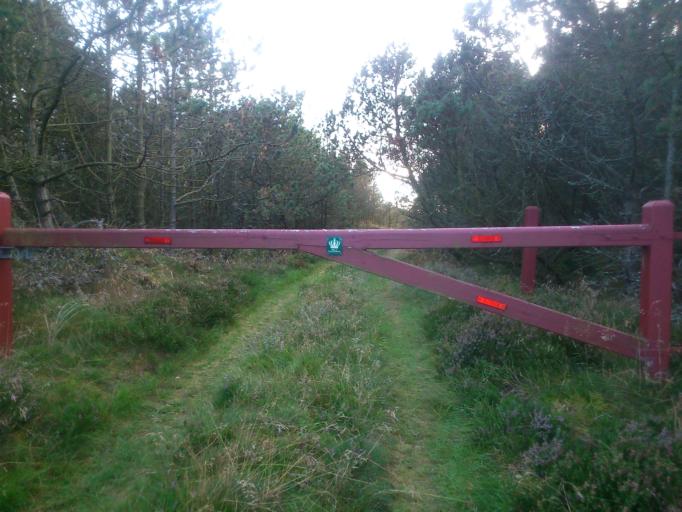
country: DK
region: South Denmark
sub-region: Varde Kommune
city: Oksbol
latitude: 55.6887
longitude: 8.1620
